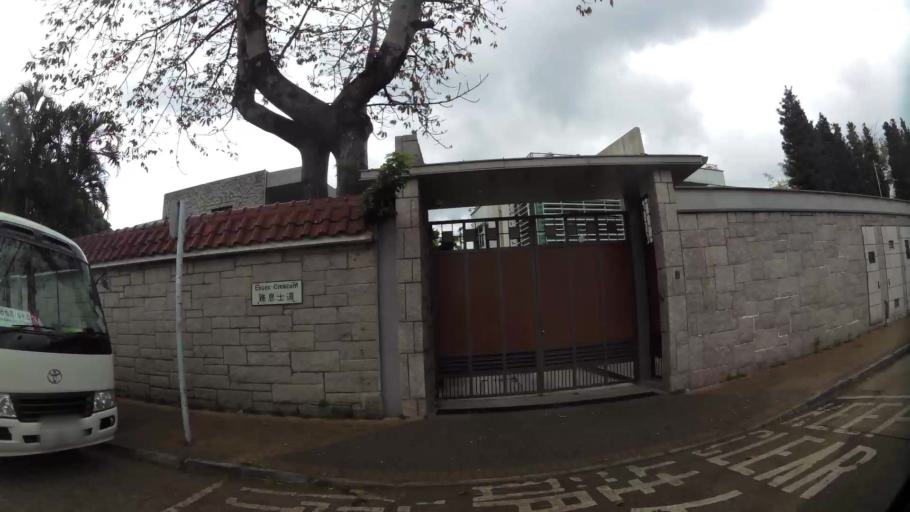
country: HK
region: Kowloon City
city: Kowloon
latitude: 22.3289
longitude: 114.1772
